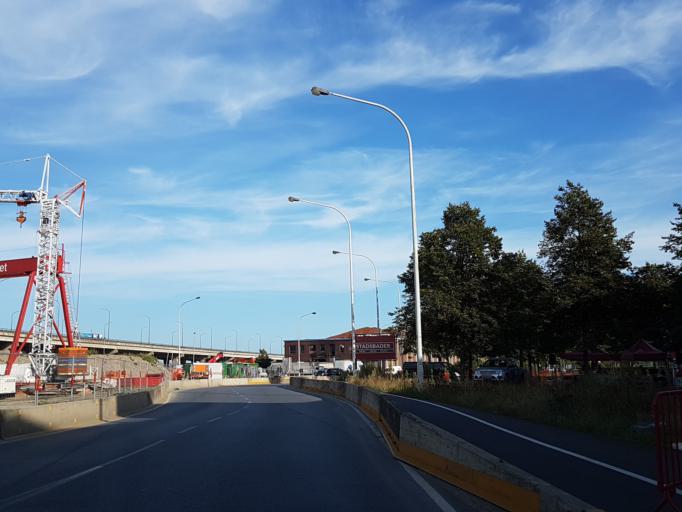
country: BE
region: Flanders
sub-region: Provincie Antwerpen
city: Antwerpen
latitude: 51.2350
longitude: 4.4282
